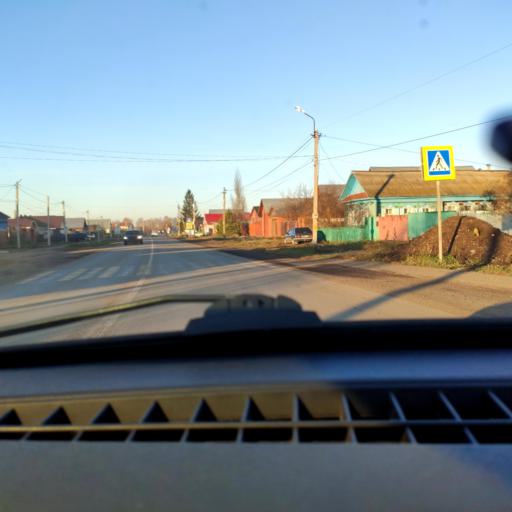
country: RU
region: Bashkortostan
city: Ufa
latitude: 54.6115
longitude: 55.9006
